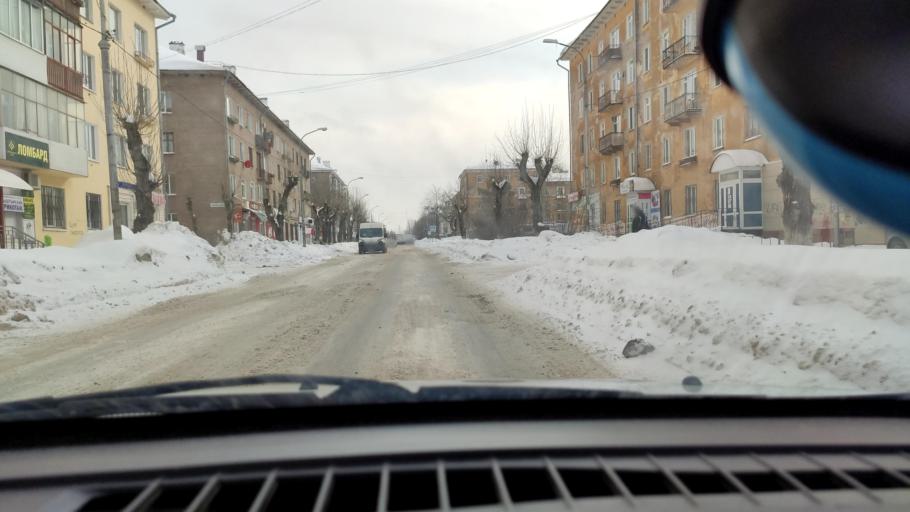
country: RU
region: Perm
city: Krasnokamsk
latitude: 58.0819
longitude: 55.7528
